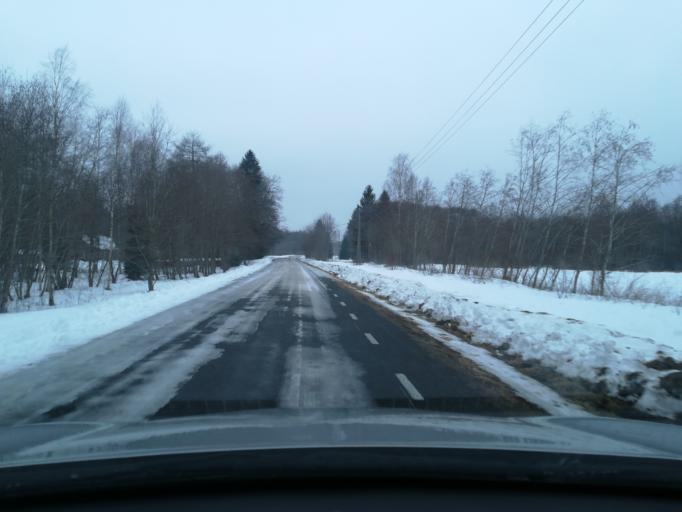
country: EE
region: Harju
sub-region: Loksa linn
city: Loksa
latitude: 59.4681
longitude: 25.7000
